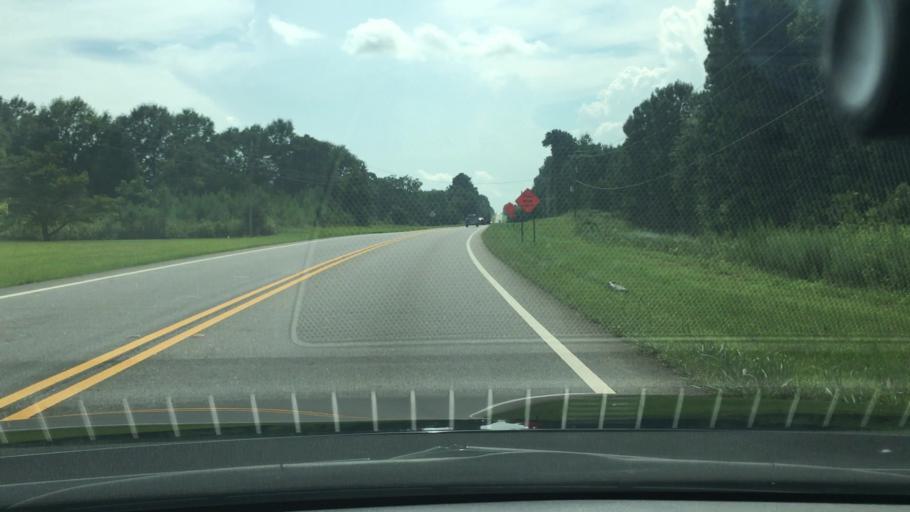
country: US
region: Georgia
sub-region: Coweta County
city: East Newnan
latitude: 33.3328
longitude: -84.7567
